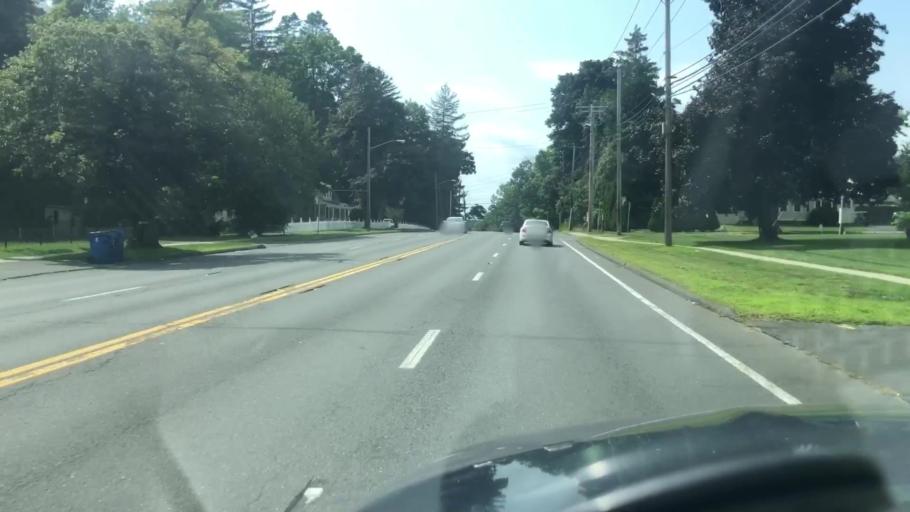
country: US
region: Massachusetts
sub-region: Hampden County
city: West Springfield
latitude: 42.1042
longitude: -72.6690
